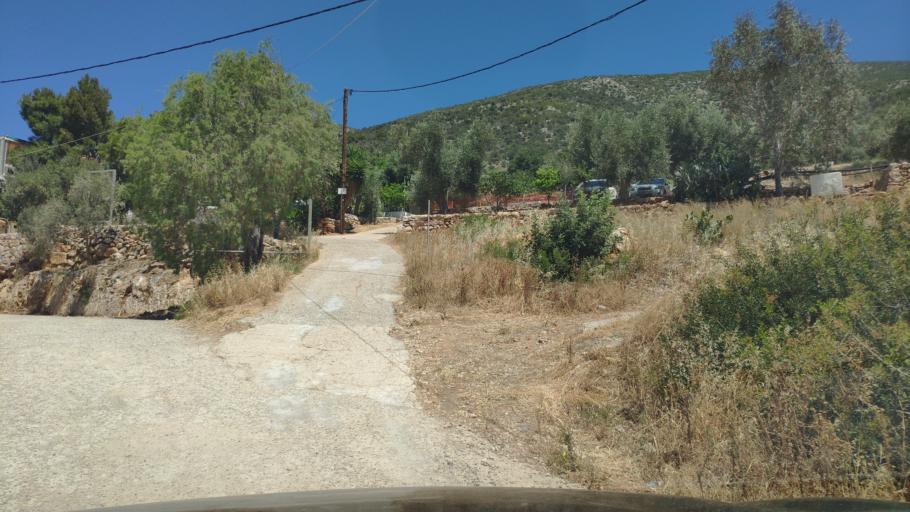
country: GR
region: Central Greece
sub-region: Nomos Voiotias
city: Kaparellion
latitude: 38.1834
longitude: 23.1430
